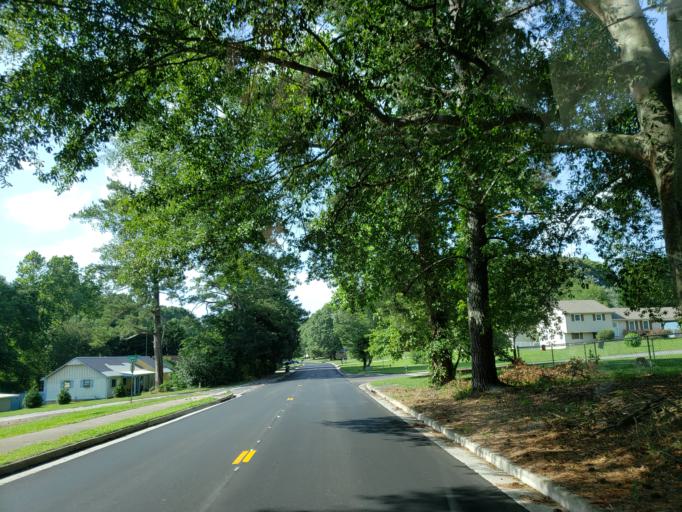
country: US
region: Georgia
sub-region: Cobb County
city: Powder Springs
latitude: 33.9063
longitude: -84.6864
